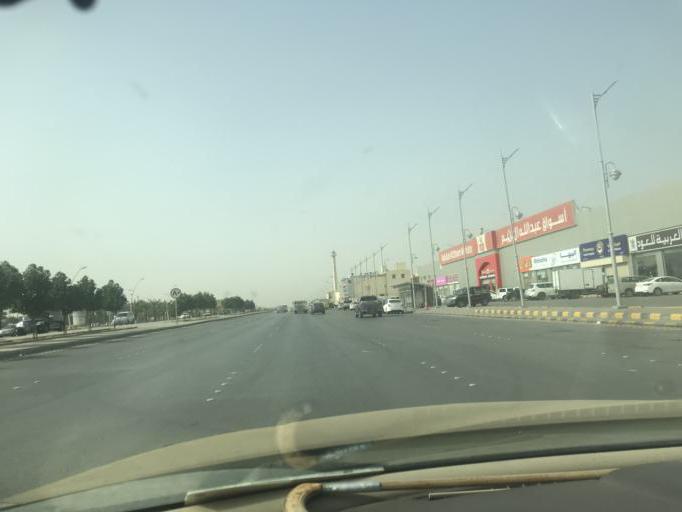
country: SA
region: Ar Riyad
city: Riyadh
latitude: 24.6685
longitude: 46.8061
